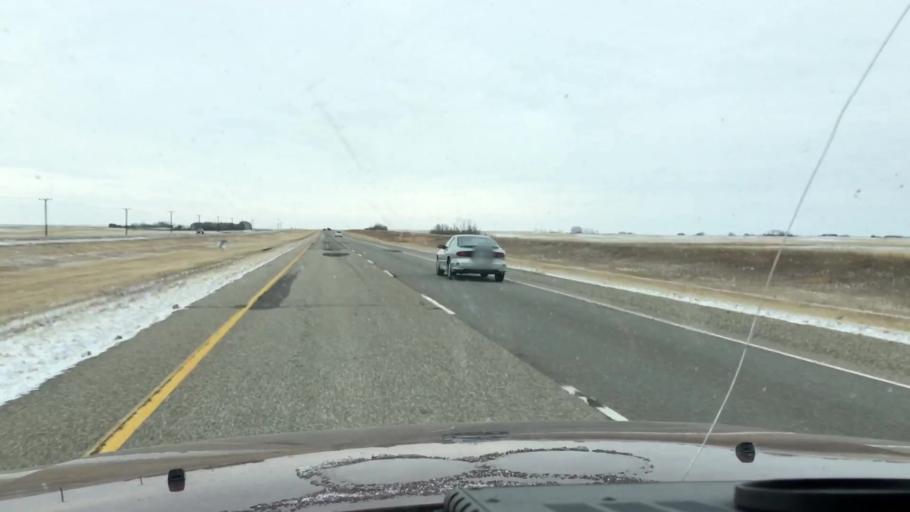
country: CA
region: Saskatchewan
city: Watrous
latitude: 51.4269
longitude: -106.1977
